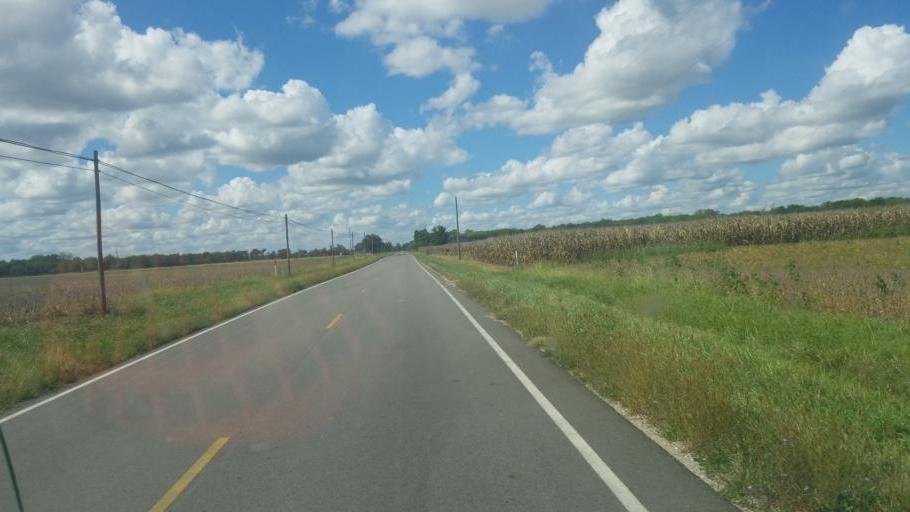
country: US
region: Ohio
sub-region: Union County
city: Marysville
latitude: 40.1862
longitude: -83.4572
